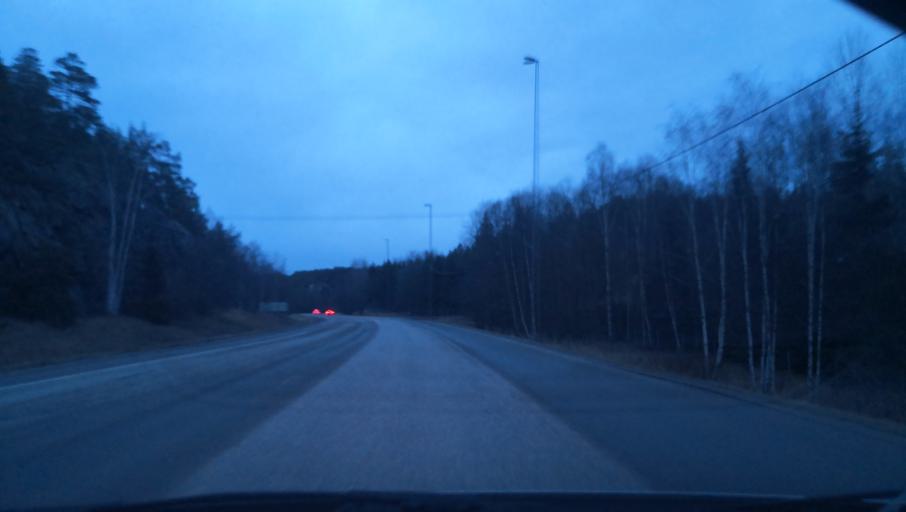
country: SE
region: Stockholm
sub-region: Nacka Kommun
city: Boo
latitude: 59.3275
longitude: 18.3346
